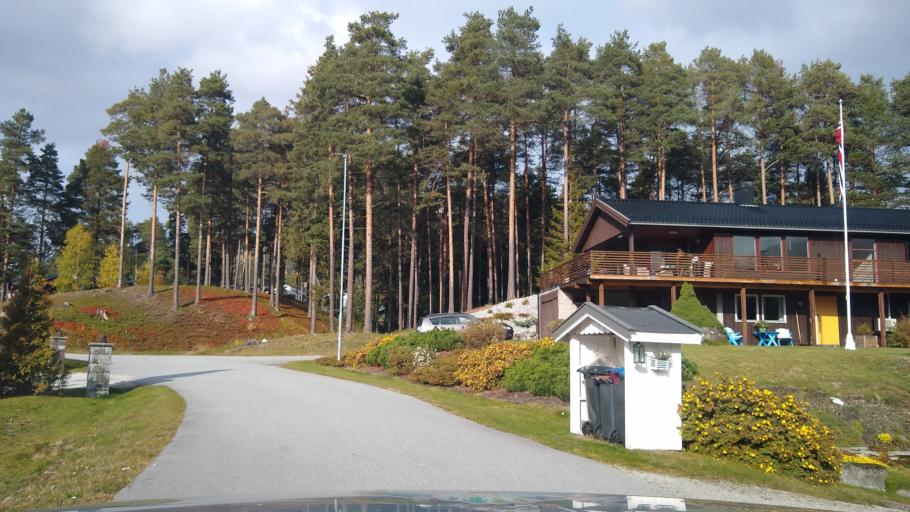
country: NO
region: Oppland
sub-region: Ringebu
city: Ringebu
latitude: 61.5375
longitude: 10.1387
